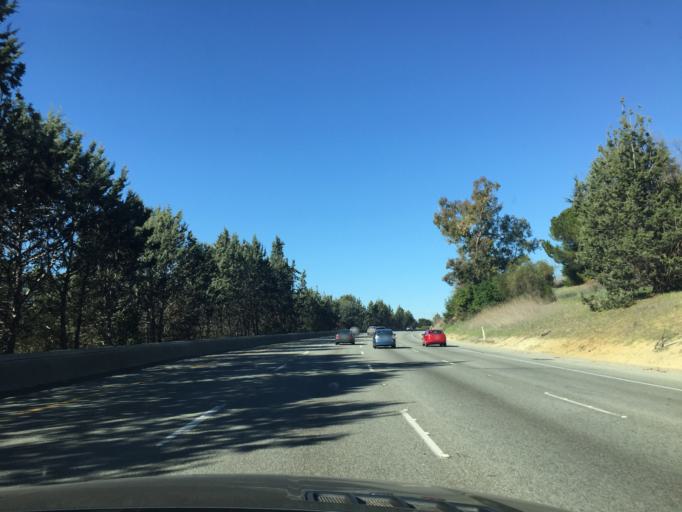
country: US
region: California
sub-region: Santa Clara County
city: Loyola
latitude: 37.3560
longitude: -122.1151
